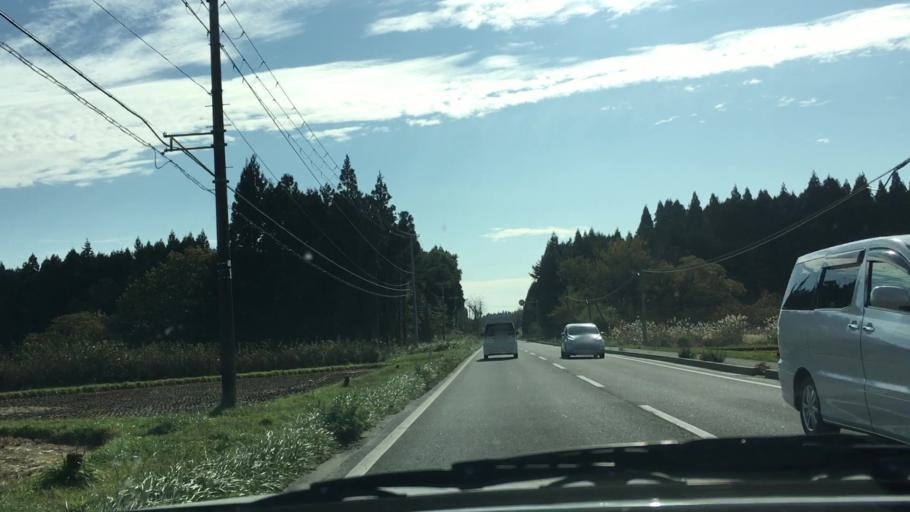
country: JP
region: Aomori
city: Hachinohe
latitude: 40.4334
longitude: 141.6883
